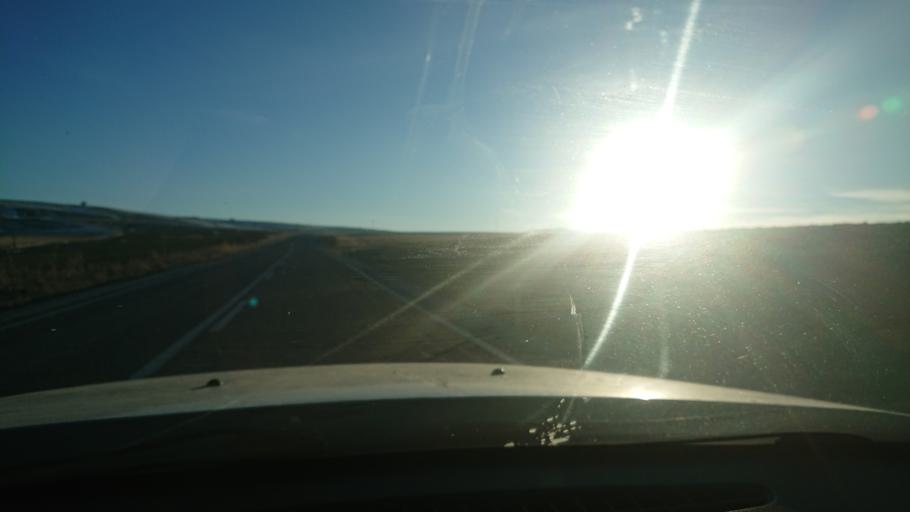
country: TR
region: Aksaray
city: Agacoren
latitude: 38.8481
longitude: 33.8959
